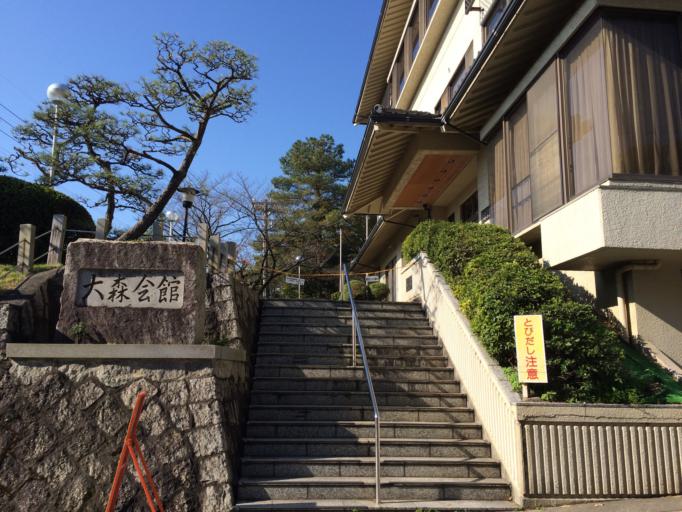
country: JP
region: Aichi
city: Kasugai
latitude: 35.2074
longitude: 136.9962
